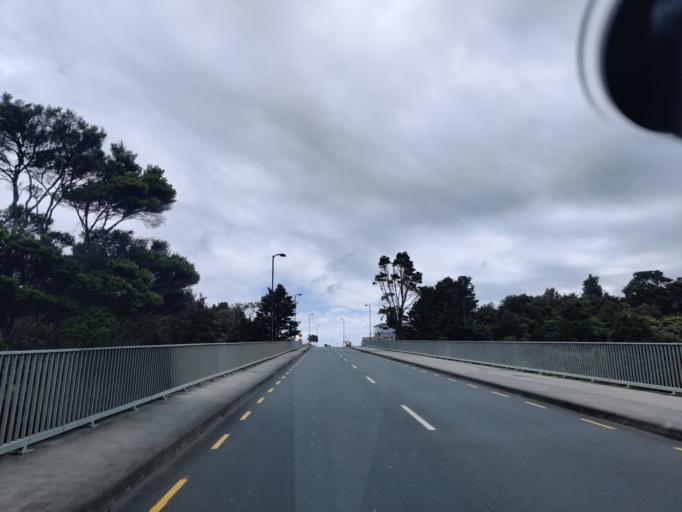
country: NZ
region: Auckland
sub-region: Auckland
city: Rothesay Bay
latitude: -36.5964
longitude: 174.6714
